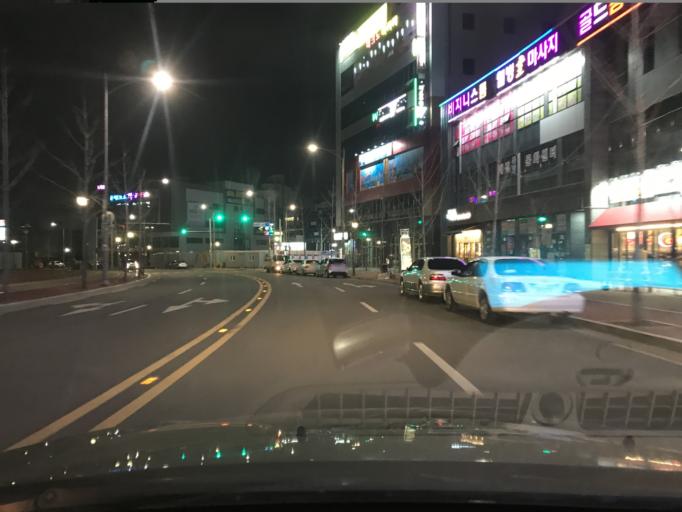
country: KR
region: Daegu
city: Hwawon
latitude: 35.6918
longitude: 128.4569
